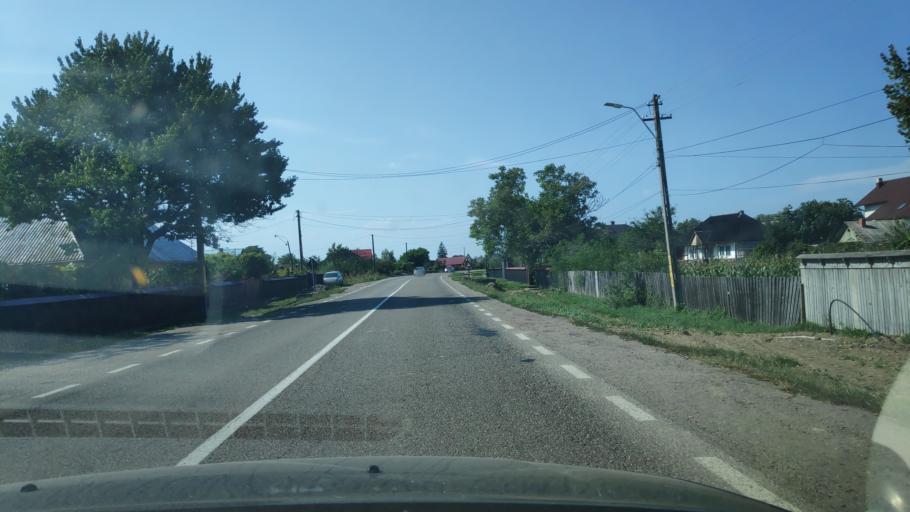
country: RO
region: Suceava
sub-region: Comuna Vadu Moldovei
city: Dumbravita
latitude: 47.3814
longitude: 26.3162
